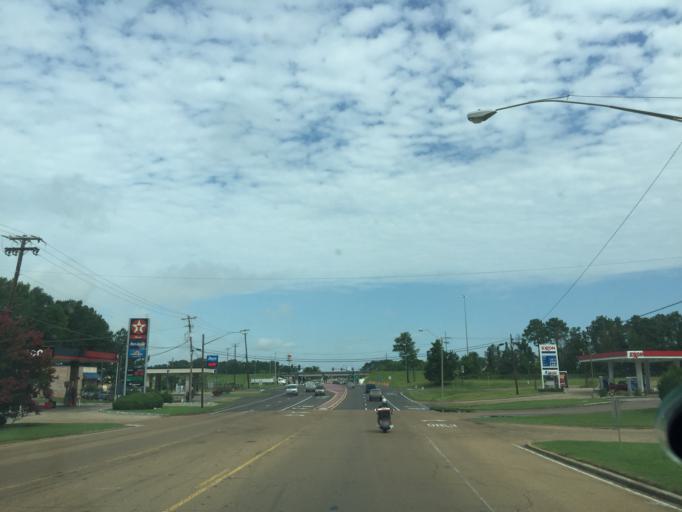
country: US
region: Mississippi
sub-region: Rankin County
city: Brandon
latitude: 32.2771
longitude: -89.9985
